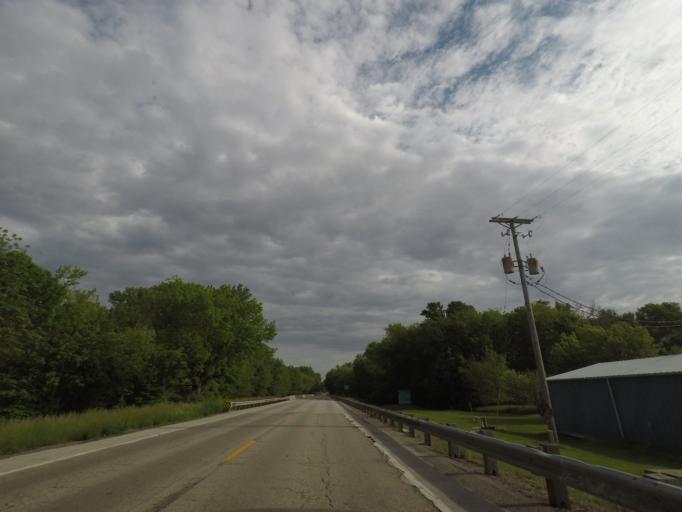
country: US
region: Illinois
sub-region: Logan County
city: Mount Pulaski
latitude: 40.0520
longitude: -89.2820
